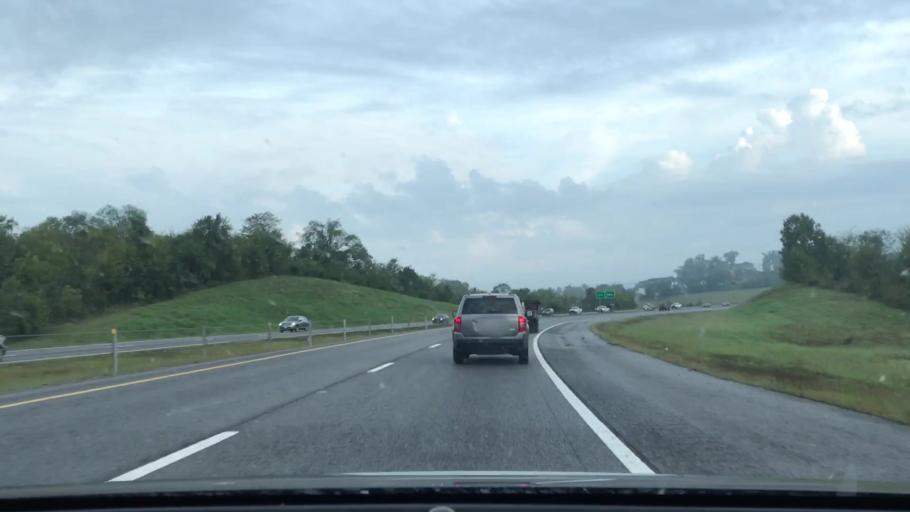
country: US
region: Tennessee
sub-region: Sumner County
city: Shackle Island
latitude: 36.3414
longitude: -86.5502
